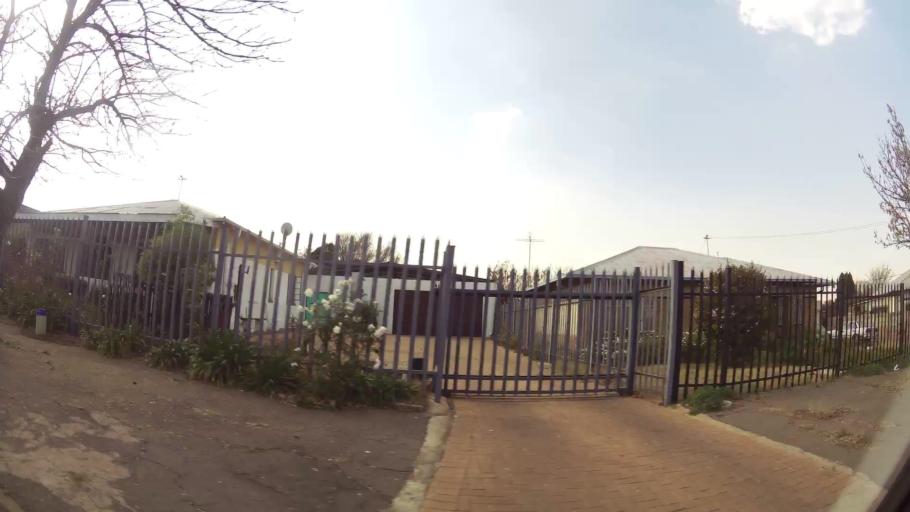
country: ZA
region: Gauteng
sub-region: Ekurhuleni Metropolitan Municipality
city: Germiston
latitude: -26.1857
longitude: 28.1833
